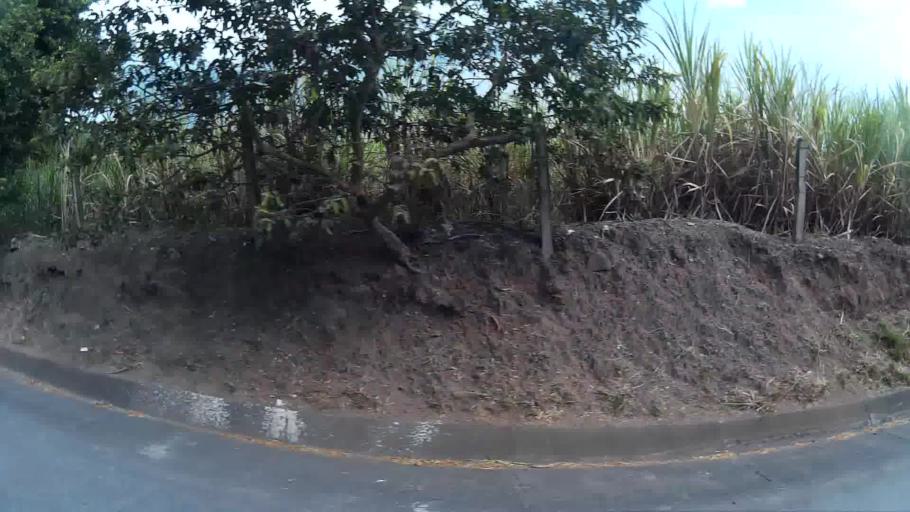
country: CO
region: Risaralda
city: Pereira
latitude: 4.8141
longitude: -75.8041
